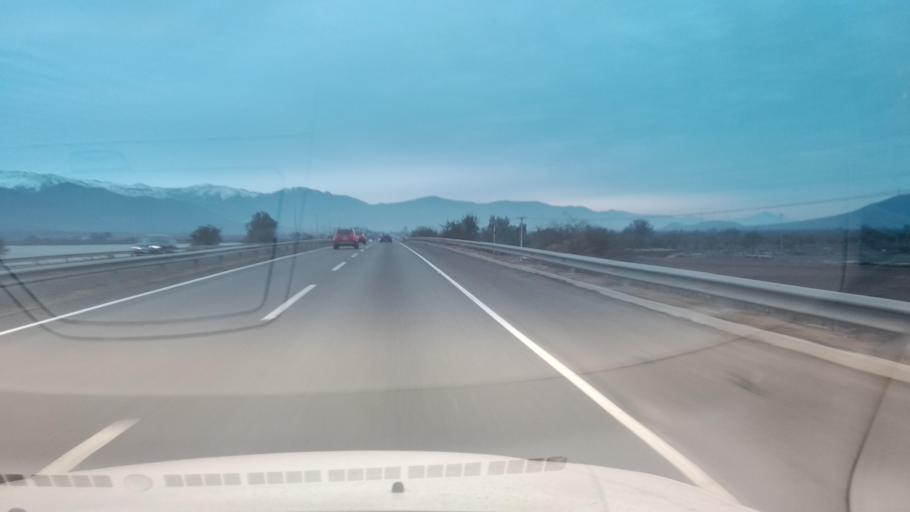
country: CL
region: Santiago Metropolitan
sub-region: Provincia de Chacabuco
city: Chicureo Abajo
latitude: -33.1452
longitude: -70.6589
